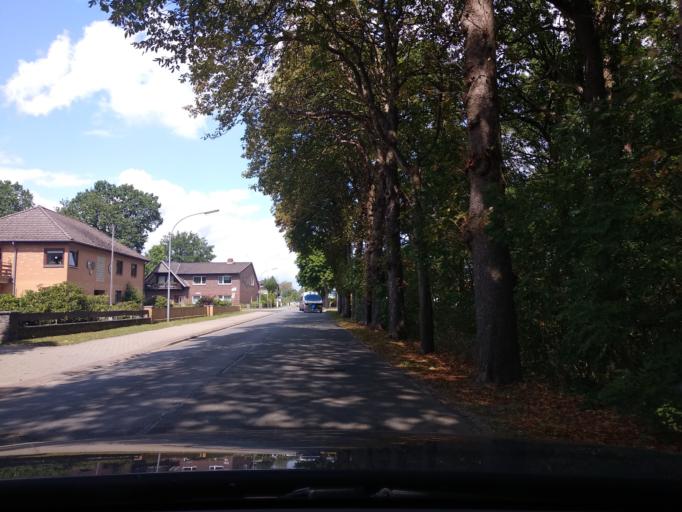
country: DE
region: Lower Saxony
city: Wagenhoff
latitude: 52.5104
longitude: 10.4819
